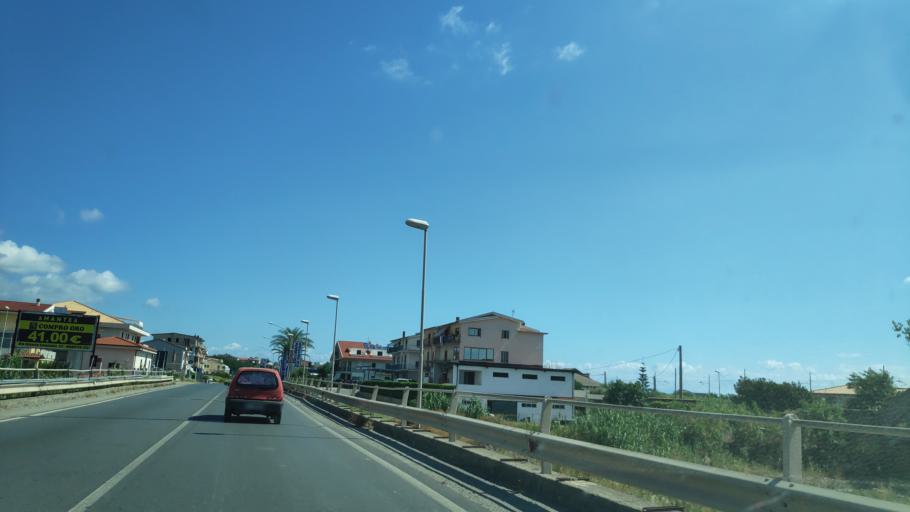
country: IT
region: Calabria
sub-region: Provincia di Cosenza
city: Campora San Giovanni
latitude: 39.0777
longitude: 16.0893
